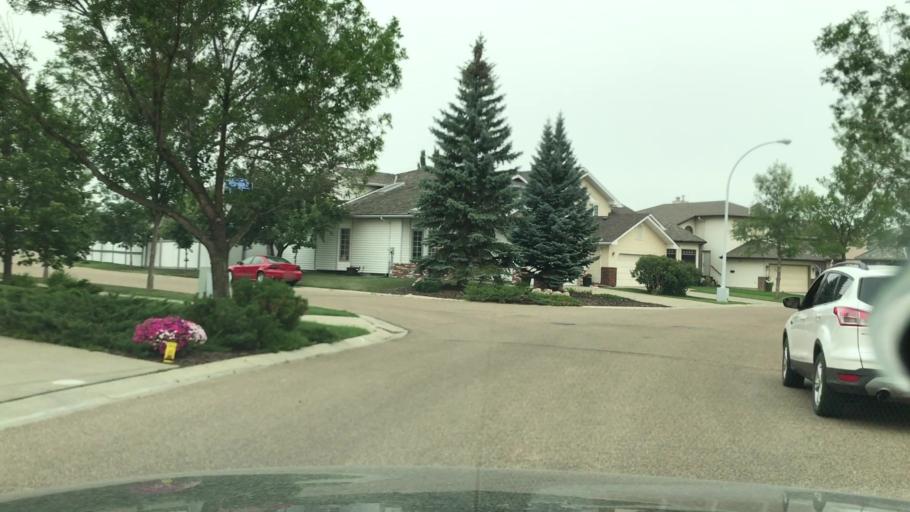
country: CA
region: Alberta
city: Edmonton
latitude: 53.4691
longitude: -113.5772
